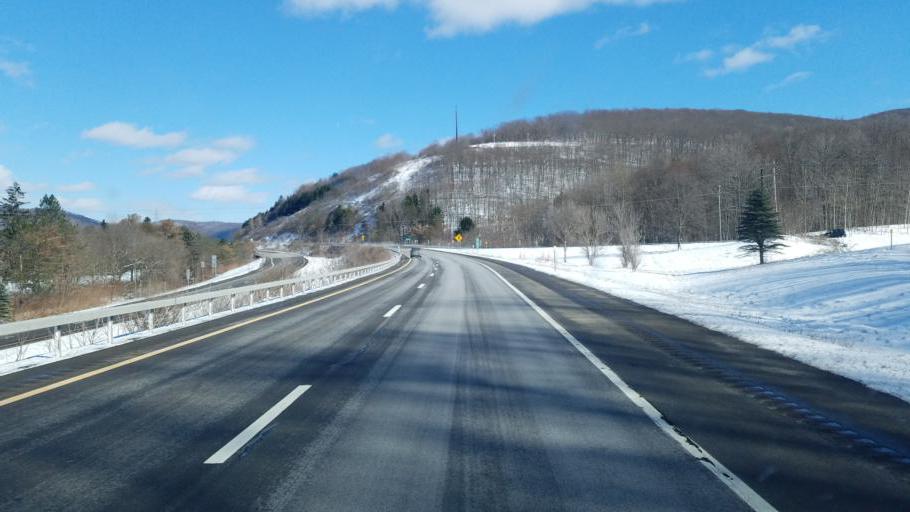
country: US
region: New York
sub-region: Cattaraugus County
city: Salamanca
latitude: 42.1494
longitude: -78.7116
